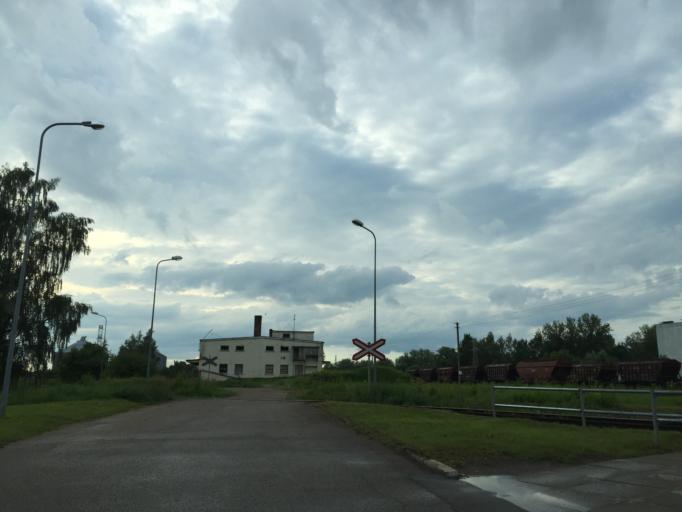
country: LV
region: Dobeles Rajons
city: Dobele
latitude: 56.6298
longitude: 23.2823
